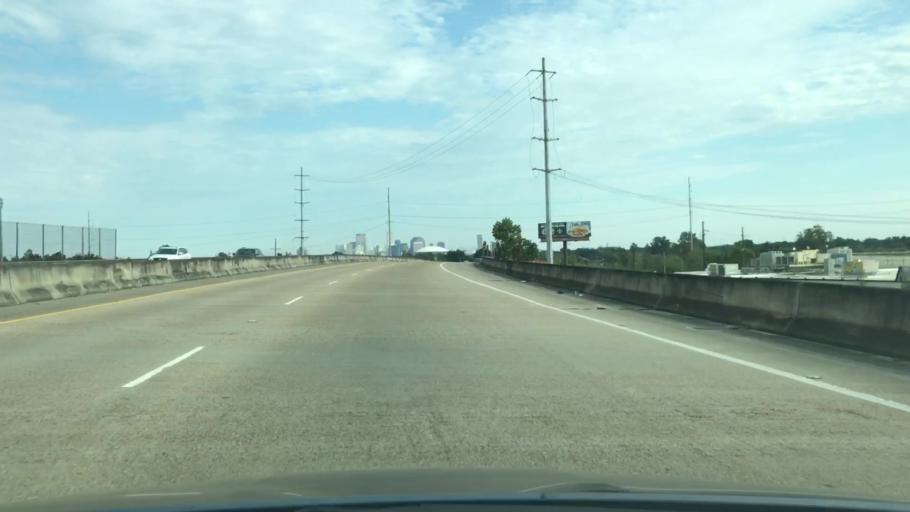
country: US
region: Louisiana
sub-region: Jefferson Parish
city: Jefferson
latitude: 29.9689
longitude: -90.1317
